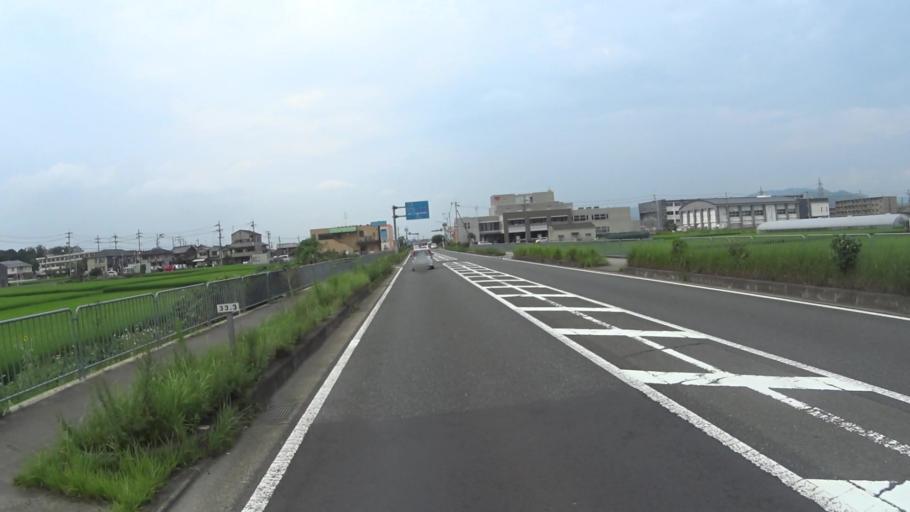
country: JP
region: Nara
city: Nara-shi
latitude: 34.7334
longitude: 135.8030
